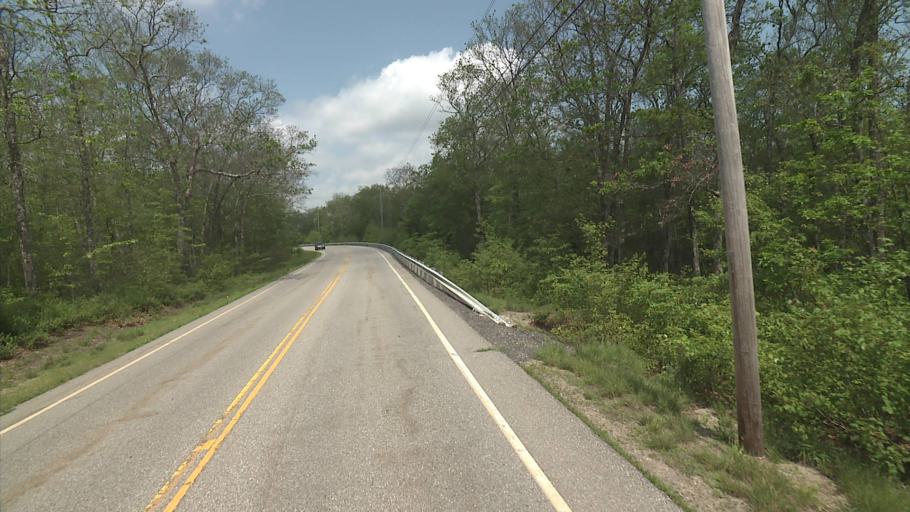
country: US
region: Rhode Island
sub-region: Washington County
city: Hope Valley
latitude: 41.5574
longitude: -71.7960
